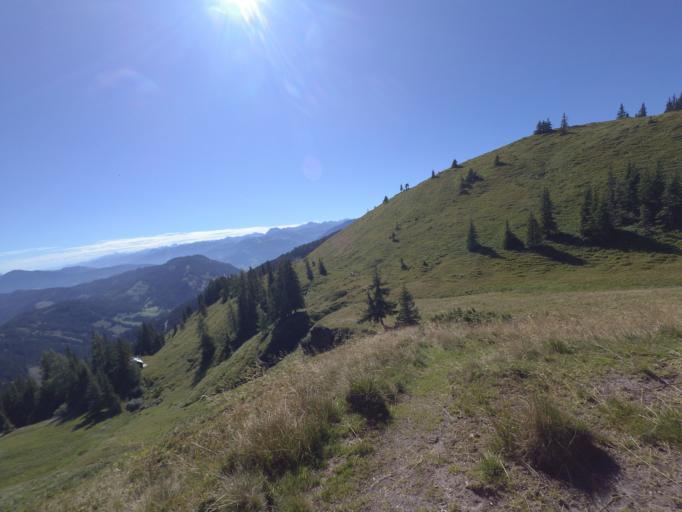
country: AT
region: Salzburg
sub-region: Politischer Bezirk Sankt Johann im Pongau
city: Goldegg
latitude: 47.3593
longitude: 13.0720
